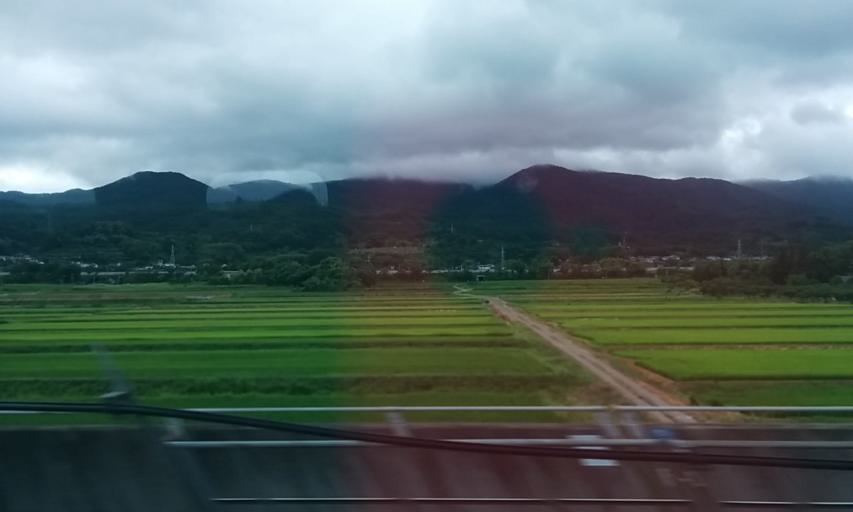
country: JP
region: Fukushima
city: Hobaramachi
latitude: 37.8691
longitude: 140.5281
